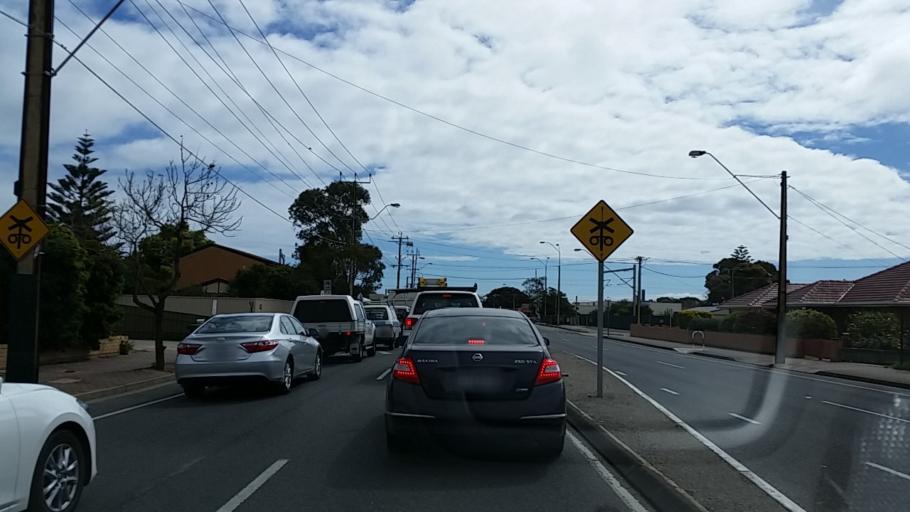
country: AU
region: South Australia
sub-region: Marion
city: Clovelly Park
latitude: -34.9934
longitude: 138.5633
